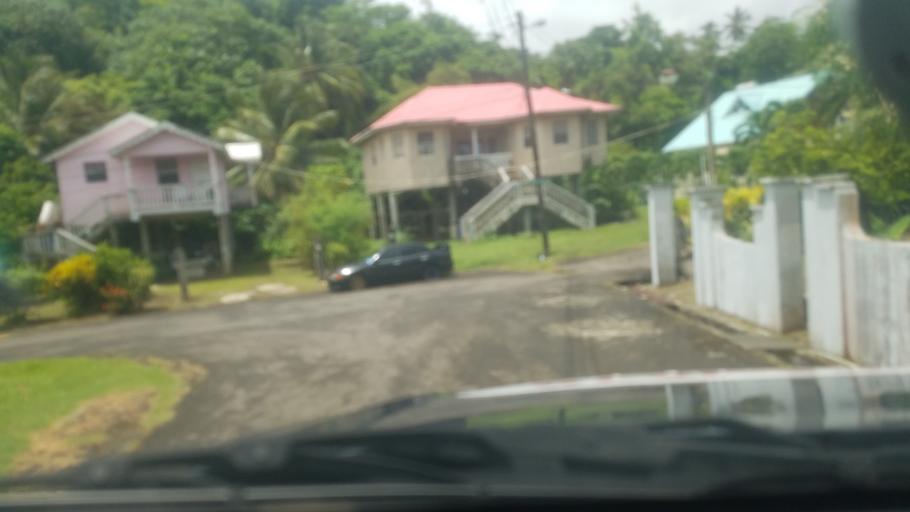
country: LC
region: Gros-Islet
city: Gros Islet
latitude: 14.0509
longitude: -60.9362
